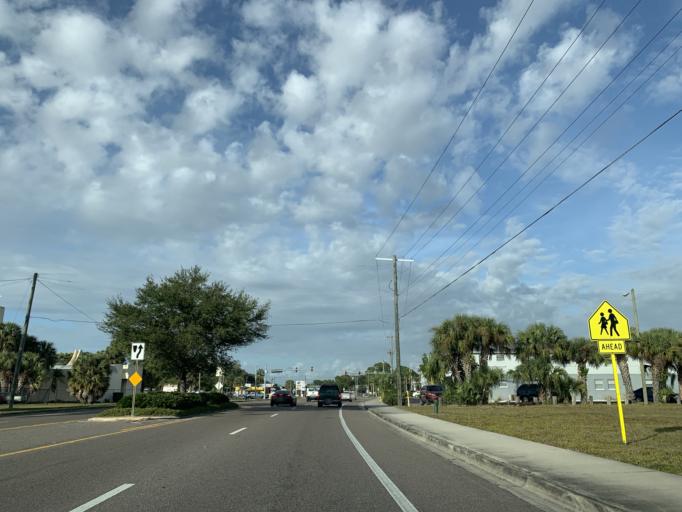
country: US
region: Florida
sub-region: Hillsborough County
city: Tampa
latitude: 27.9063
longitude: -82.5184
